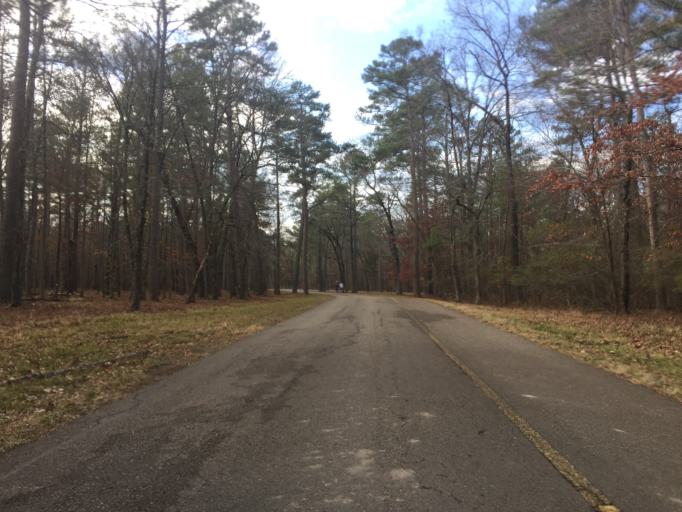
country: US
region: Georgia
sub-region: Catoosa County
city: Fort Oglethorpe
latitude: 34.9293
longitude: -85.2623
